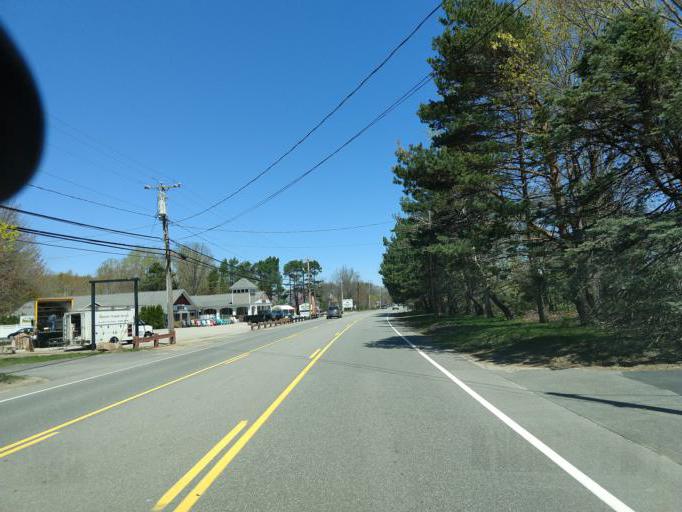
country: US
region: Maine
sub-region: York County
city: Wells Beach Station
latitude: 43.3379
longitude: -70.5672
